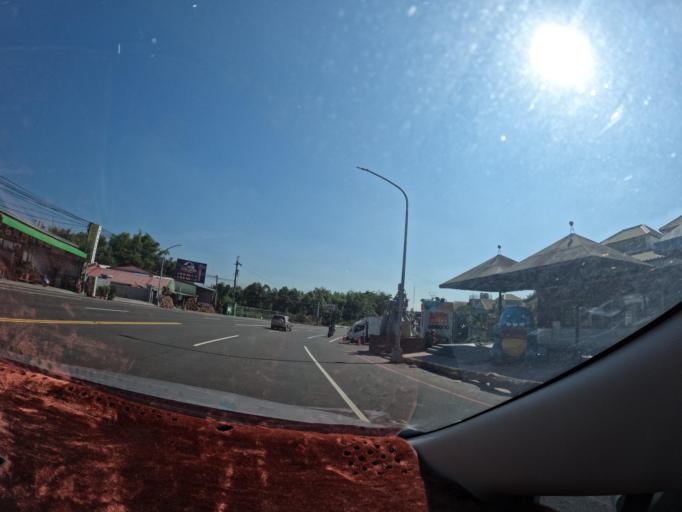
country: TW
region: Taiwan
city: Yujing
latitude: 23.0628
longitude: 120.3889
